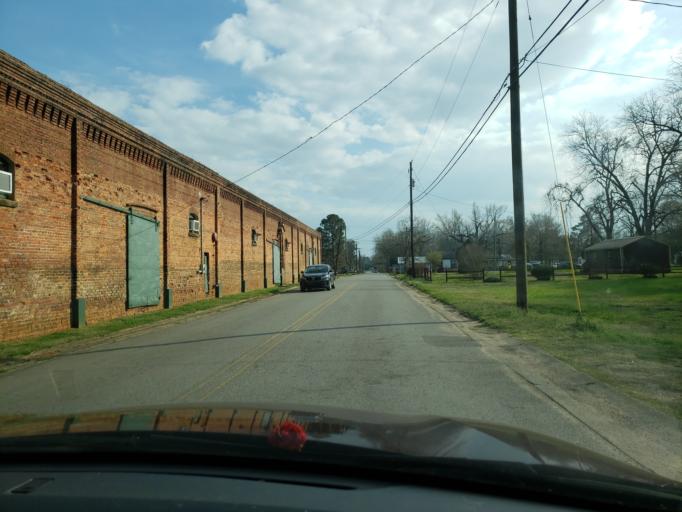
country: US
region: Alabama
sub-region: Hale County
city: Greensboro
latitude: 32.6995
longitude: -87.6093
